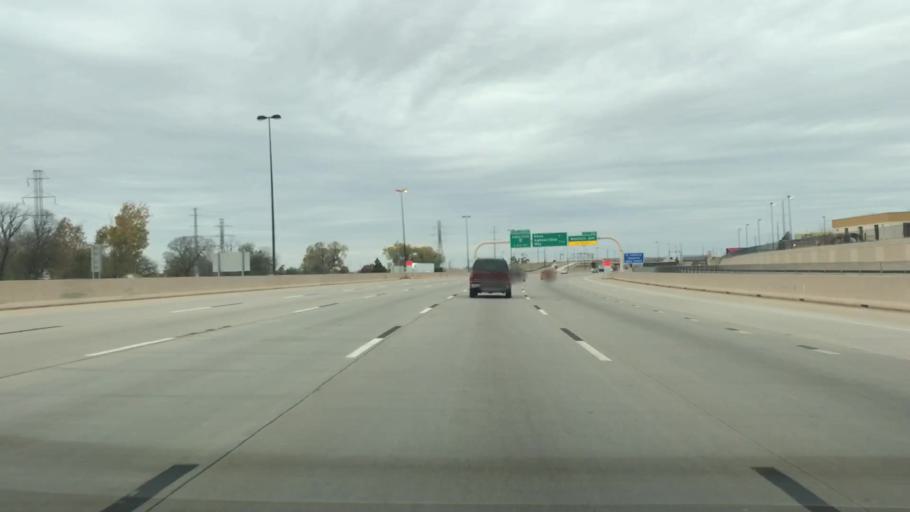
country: US
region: Oklahoma
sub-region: Oklahoma County
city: Oklahoma City
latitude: 35.4565
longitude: -97.5213
